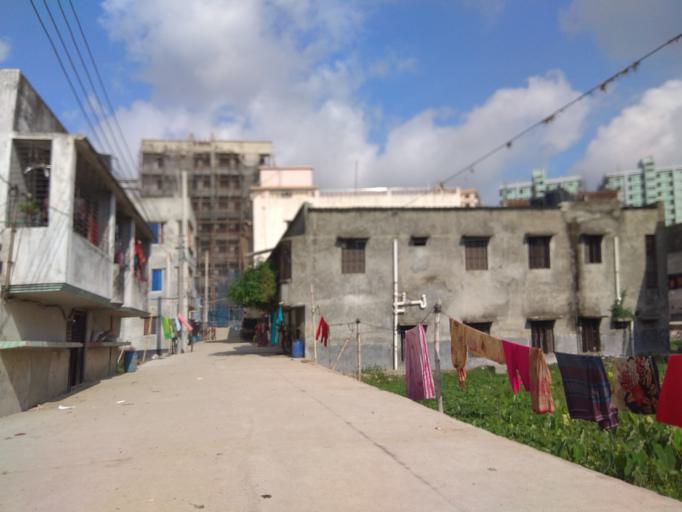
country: BD
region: Dhaka
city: Paltan
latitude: 23.8076
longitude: 90.3844
